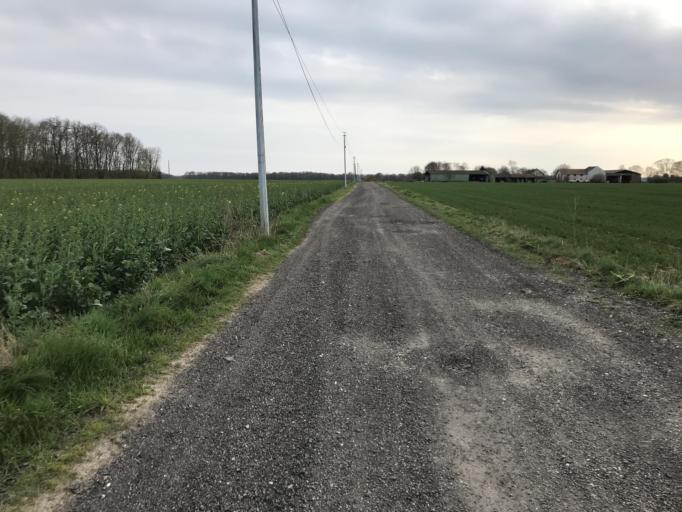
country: FR
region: Ile-de-France
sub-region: Departement de l'Essonne
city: Les Molieres
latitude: 48.6621
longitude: 2.0503
